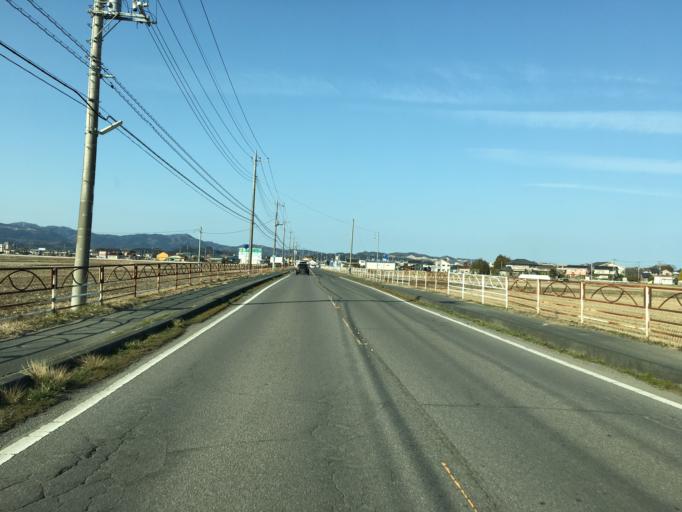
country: JP
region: Ibaraki
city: Kitaibaraki
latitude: 36.7689
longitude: 140.7329
